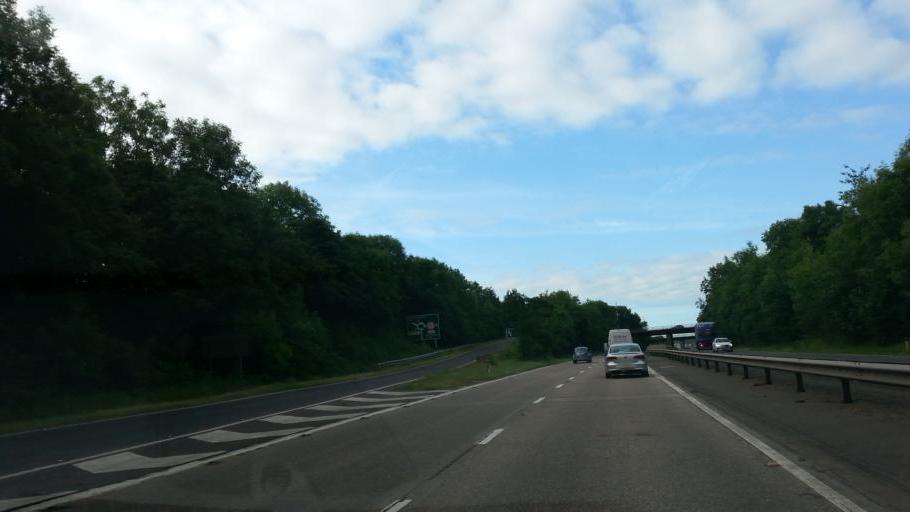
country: GB
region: England
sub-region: Nottinghamshire
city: Cotgrave
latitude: 52.8551
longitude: -1.0313
